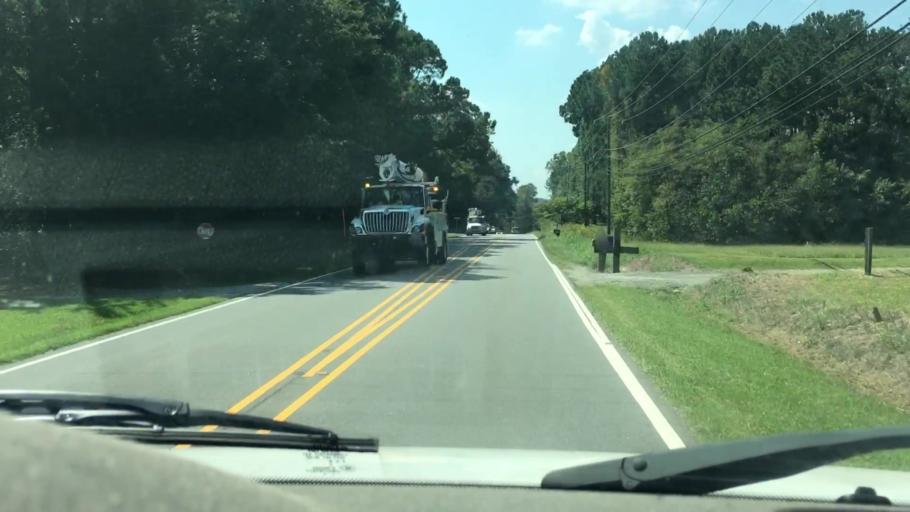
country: US
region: North Carolina
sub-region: Mecklenburg County
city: Huntersville
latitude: 35.3504
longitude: -80.8791
